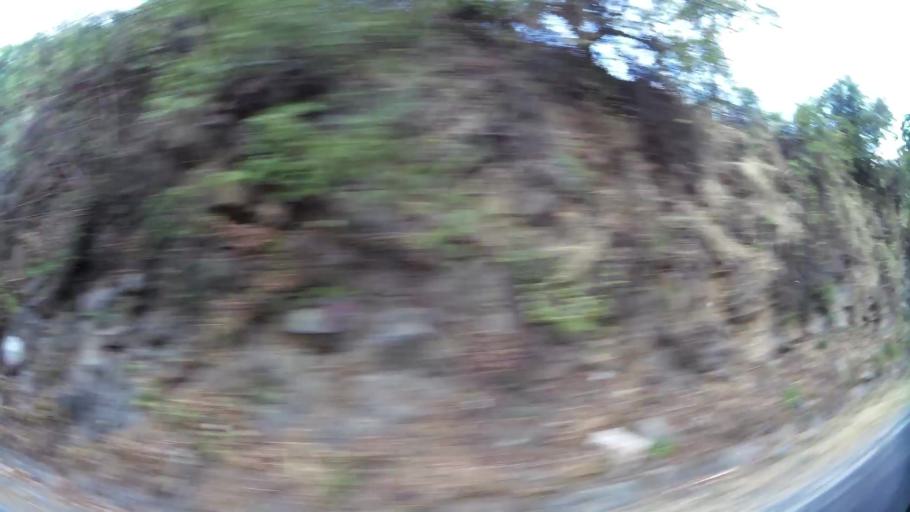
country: SV
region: San Vicente
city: Apastepeque
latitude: 13.6628
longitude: -88.7936
